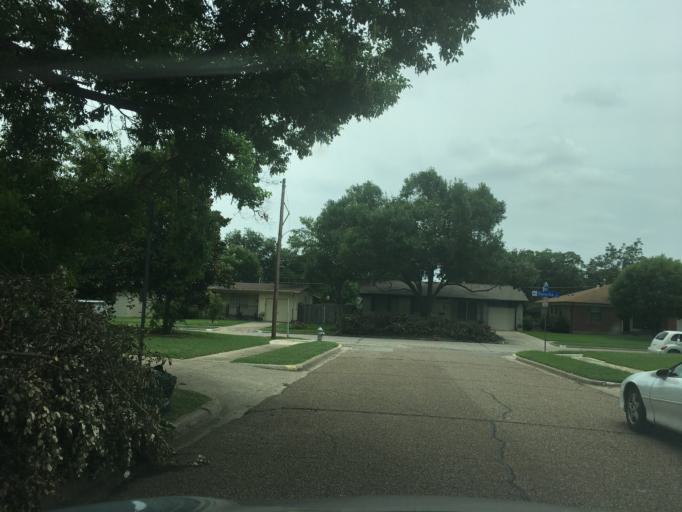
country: US
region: Texas
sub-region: Dallas County
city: Richardson
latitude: 32.9501
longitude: -96.7612
